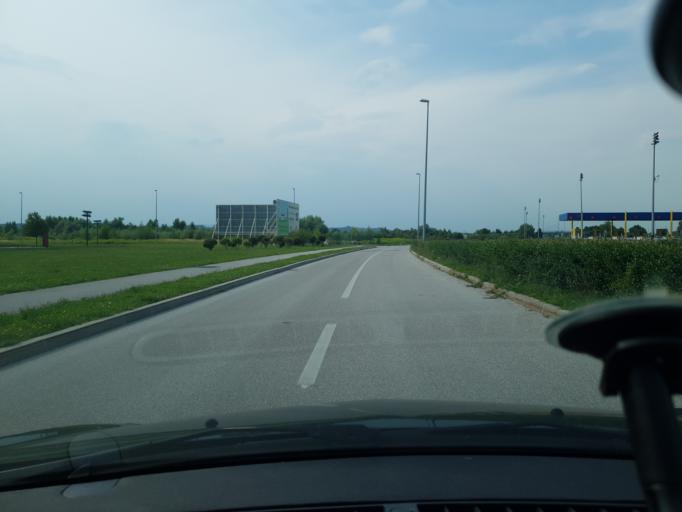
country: HR
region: Zagrebacka
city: Jablanovec
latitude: 45.8729
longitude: 15.8293
